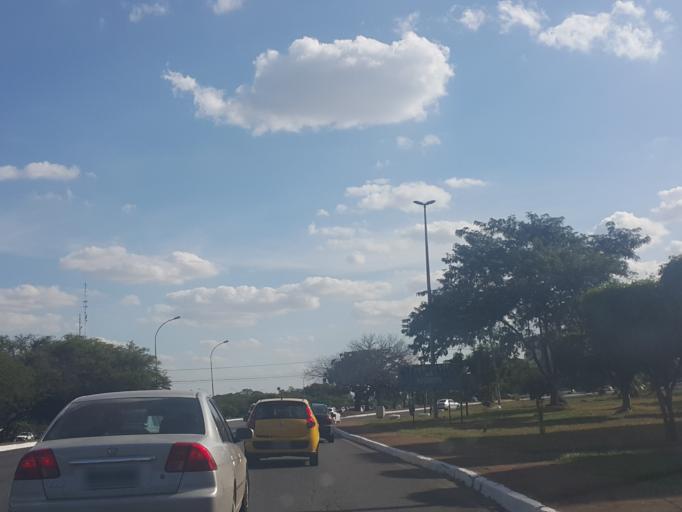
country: BR
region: Federal District
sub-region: Brasilia
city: Brasilia
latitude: -15.8059
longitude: -47.9272
